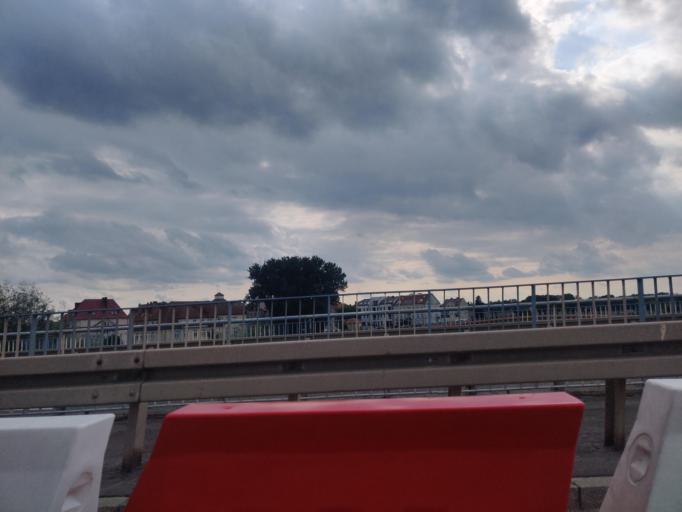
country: PL
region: Greater Poland Voivodeship
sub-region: Konin
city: Konin
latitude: 52.2139
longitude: 18.2578
